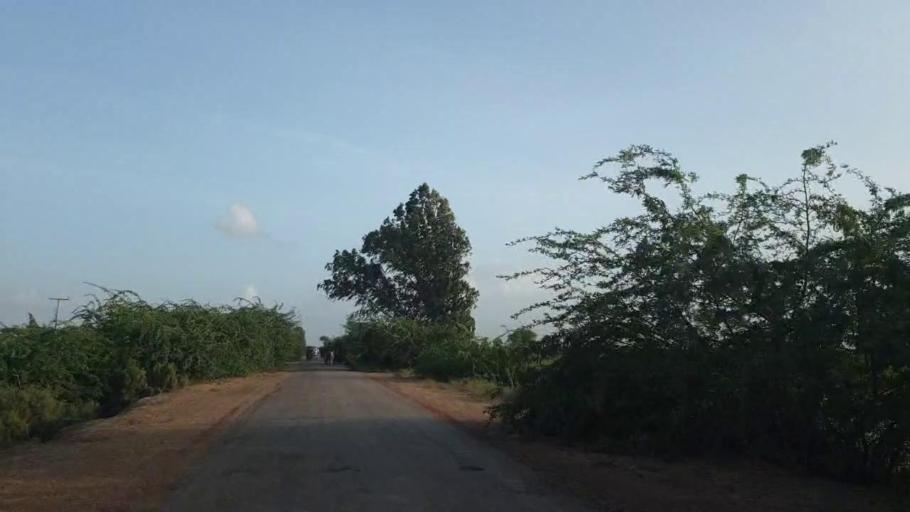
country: PK
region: Sindh
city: Kadhan
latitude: 24.6121
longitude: 69.1158
